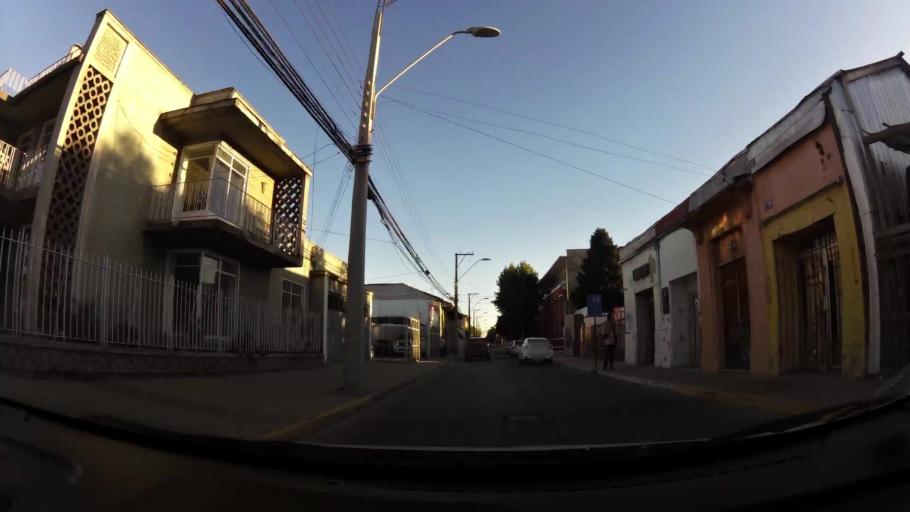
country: CL
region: Maule
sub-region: Provincia de Curico
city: Curico
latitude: -34.9872
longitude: -71.2398
